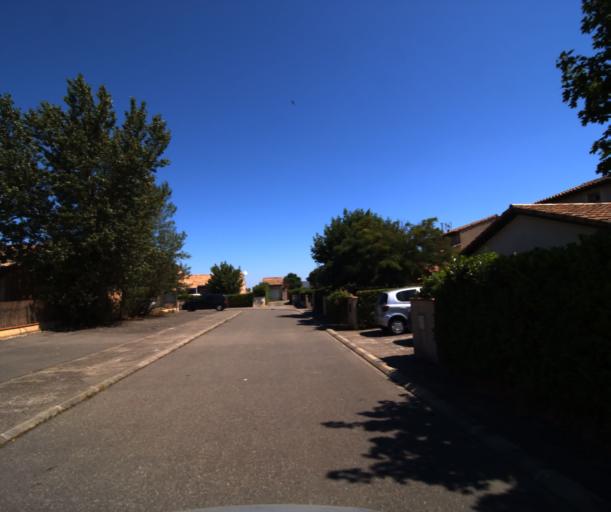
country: FR
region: Midi-Pyrenees
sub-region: Departement de la Haute-Garonne
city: Seysses
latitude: 43.4692
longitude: 1.3125
